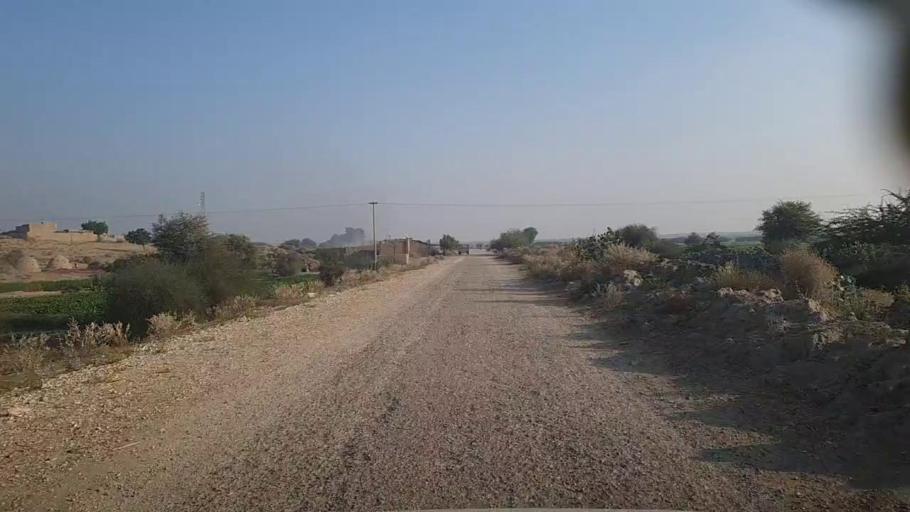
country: PK
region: Sindh
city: Karaundi
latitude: 26.7227
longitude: 68.4912
